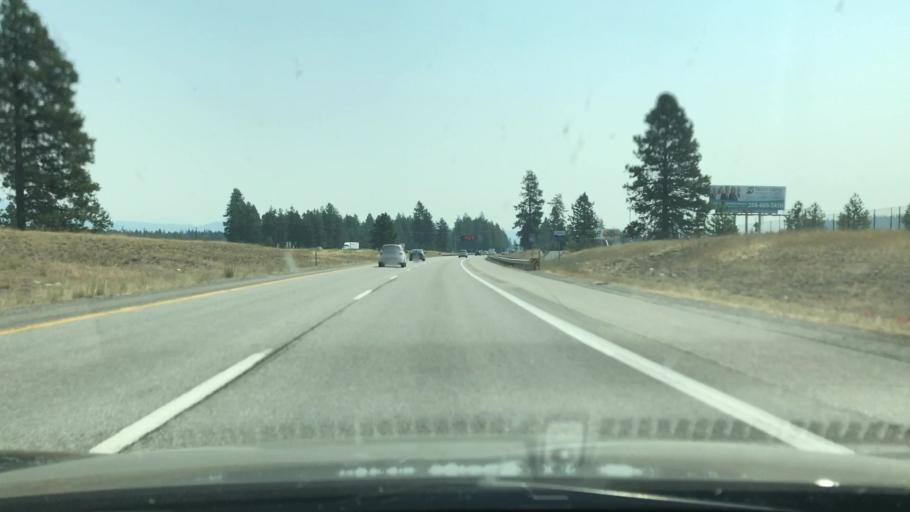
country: US
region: Idaho
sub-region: Kootenai County
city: Coeur d'Alene
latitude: 47.7081
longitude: -116.8561
